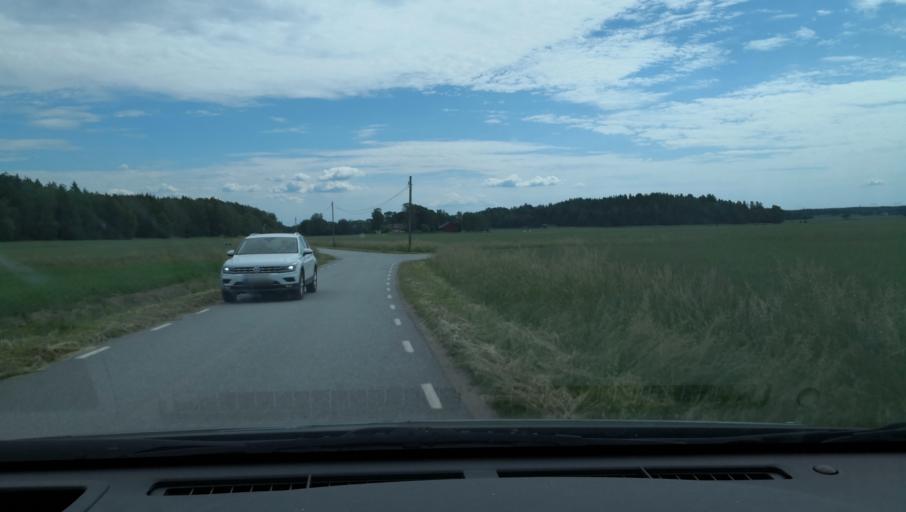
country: SE
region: Uppsala
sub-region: Enkopings Kommun
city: Orsundsbro
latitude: 59.6984
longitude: 17.4338
